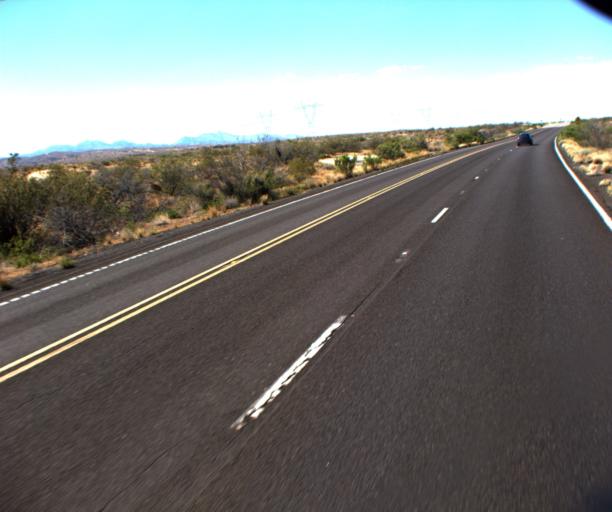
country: US
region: Arizona
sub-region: Mohave County
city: Kingman
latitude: 34.9443
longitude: -113.6664
